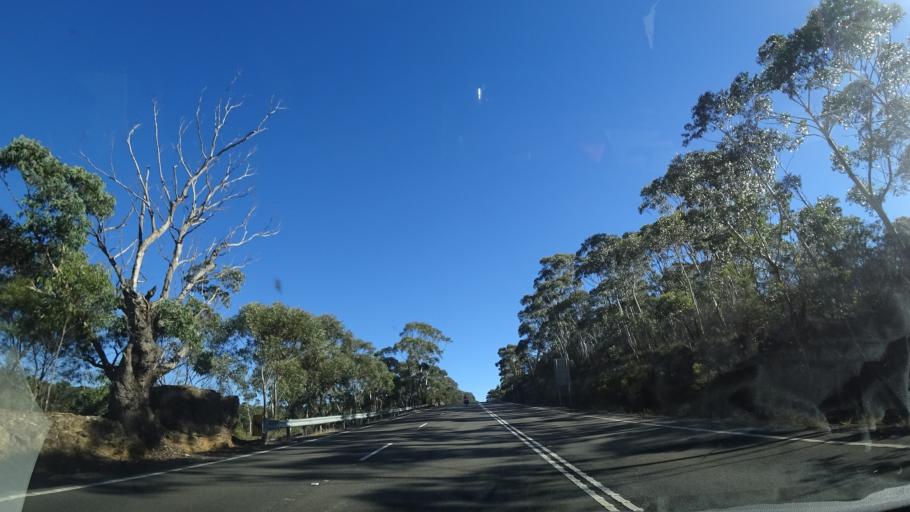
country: AU
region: New South Wales
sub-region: Blue Mountains Municipality
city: Blackheath
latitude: -33.5518
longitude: 150.3384
